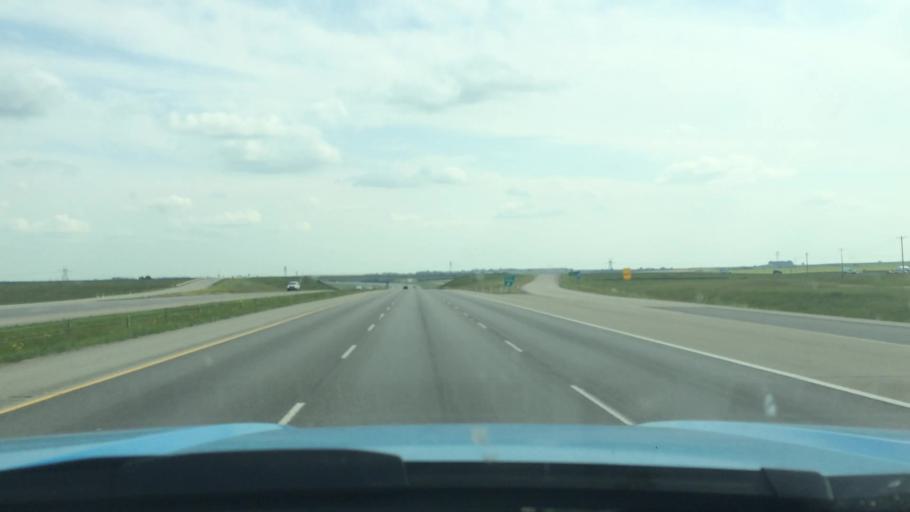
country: CA
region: Alberta
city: Crossfield
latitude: 51.4785
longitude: -114.0255
